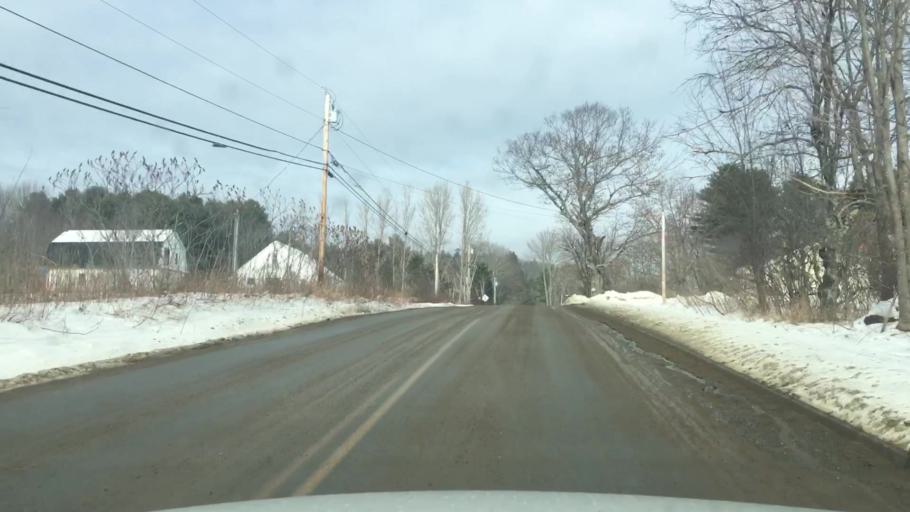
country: US
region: Maine
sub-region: Penobscot County
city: Hermon
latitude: 44.7688
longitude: -68.9604
